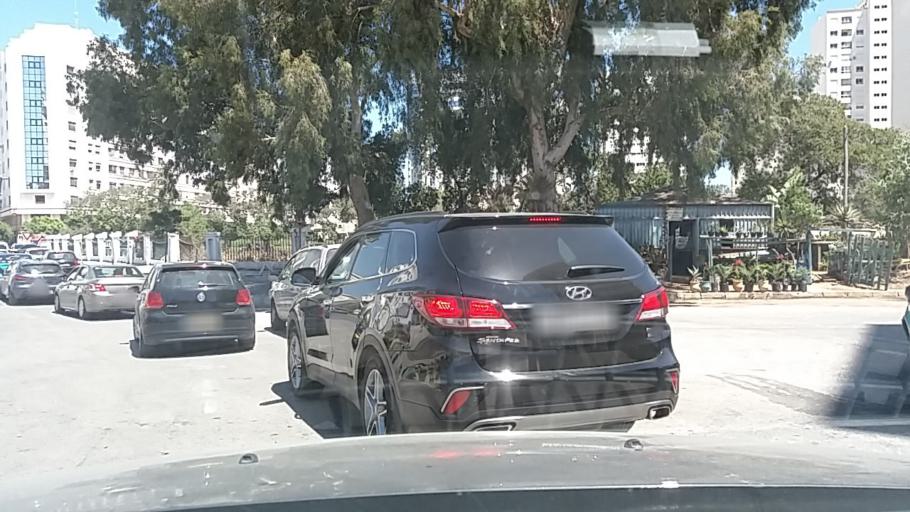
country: MA
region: Tanger-Tetouan
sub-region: Tanger-Assilah
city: Tangier
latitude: 35.7709
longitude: -5.7943
